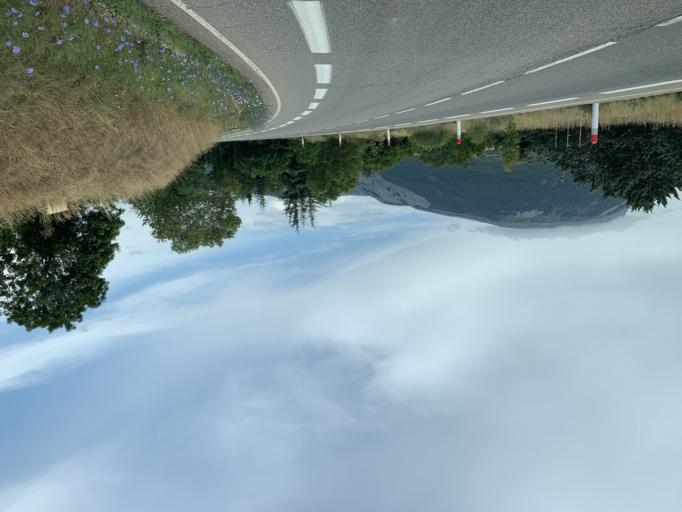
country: FR
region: Provence-Alpes-Cote d'Azur
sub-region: Departement des Hautes-Alpes
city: Gap
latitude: 44.5400
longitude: 6.0247
